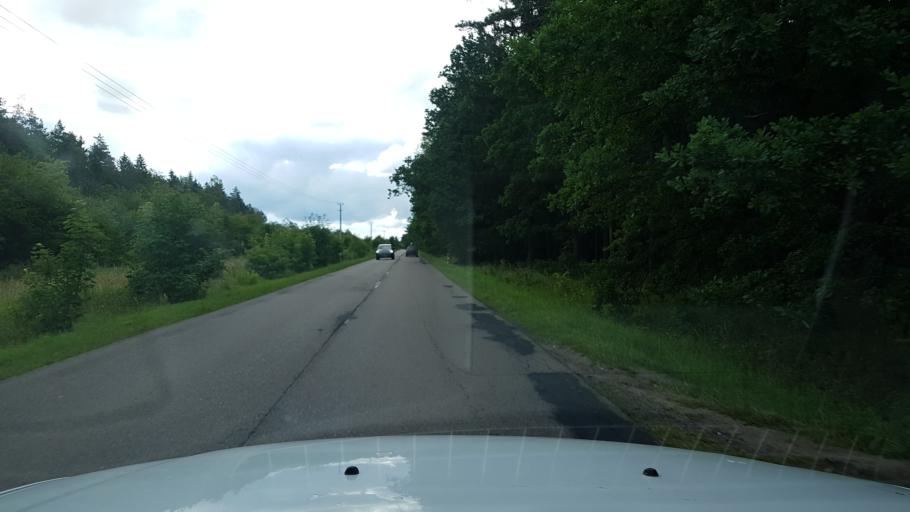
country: PL
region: West Pomeranian Voivodeship
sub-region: Powiat swidwinski
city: Rabino
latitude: 53.7773
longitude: 15.9319
